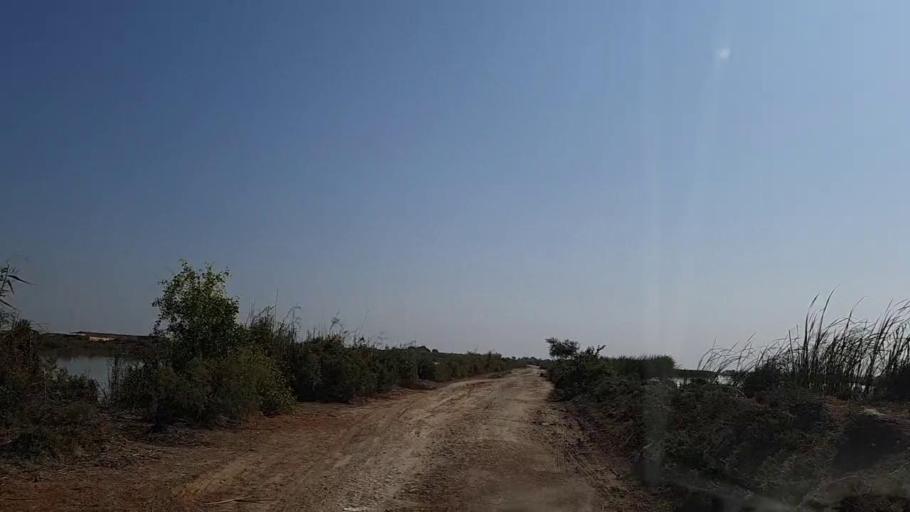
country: PK
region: Sindh
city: Chuhar Jamali
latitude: 24.4645
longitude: 68.1017
